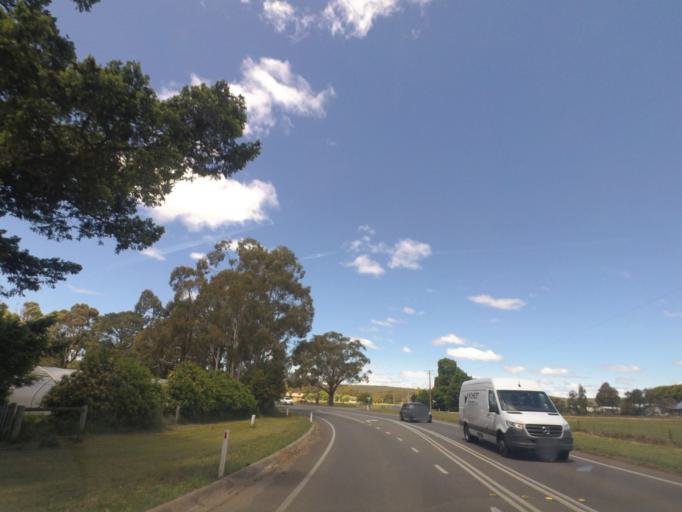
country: AU
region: Victoria
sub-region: Mount Alexander
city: Castlemaine
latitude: -37.2991
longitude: 144.2428
